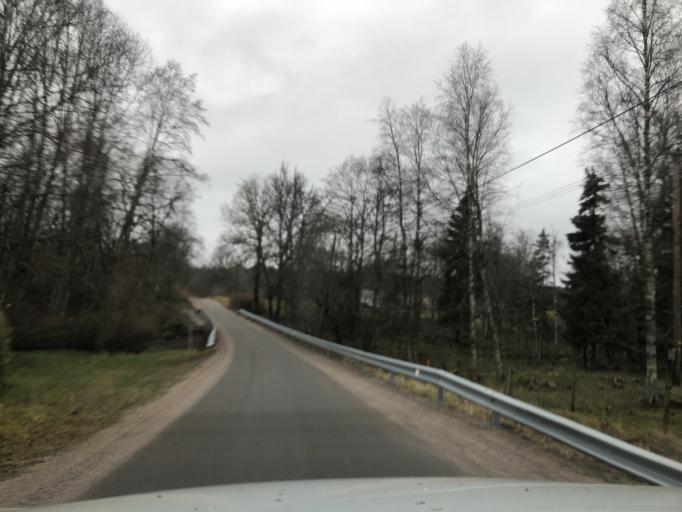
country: SE
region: Vaestra Goetaland
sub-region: Ulricehamns Kommun
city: Ulricehamn
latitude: 57.8624
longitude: 13.5732
